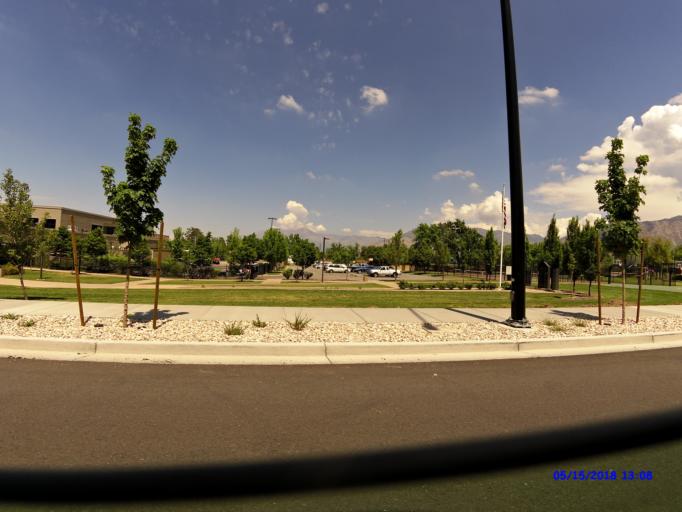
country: US
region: Utah
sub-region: Weber County
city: South Ogden
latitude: 41.1906
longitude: -111.9672
